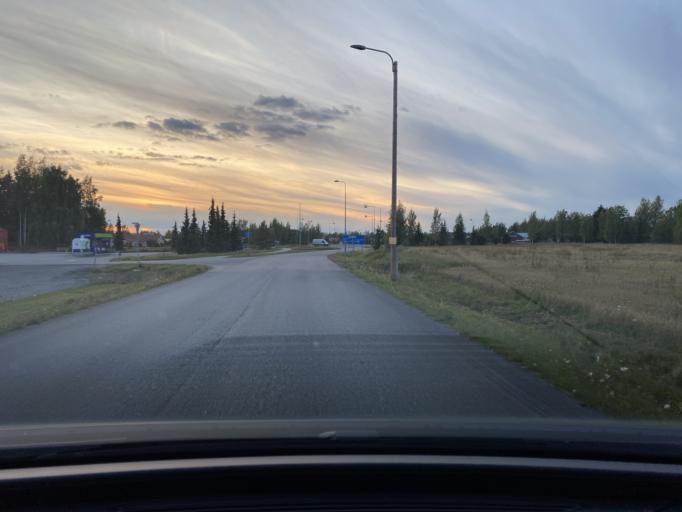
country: FI
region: Satakunta
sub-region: Pori
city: Huittinen
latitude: 61.1725
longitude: 22.7128
